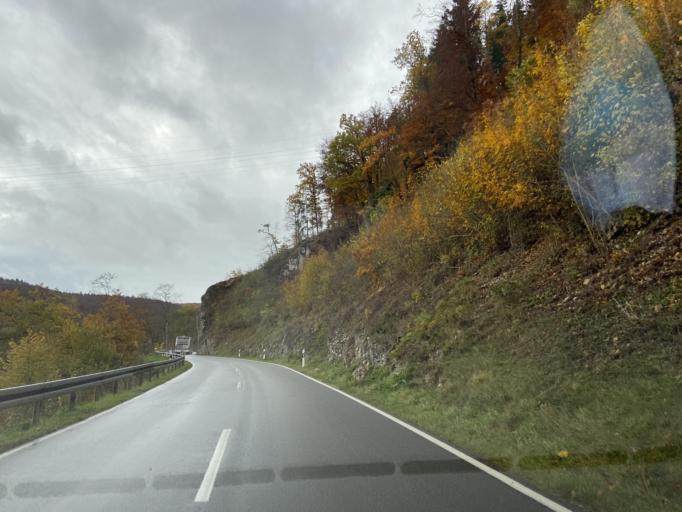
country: DE
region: Baden-Wuerttemberg
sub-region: Tuebingen Region
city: Stetten am Kalten Markt
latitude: 48.0929
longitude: 9.1003
